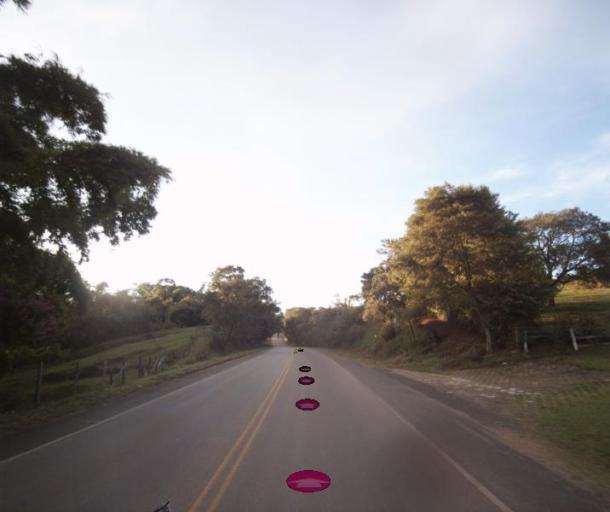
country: BR
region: Goias
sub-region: Abadiania
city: Abadiania
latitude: -16.1321
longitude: -48.8932
